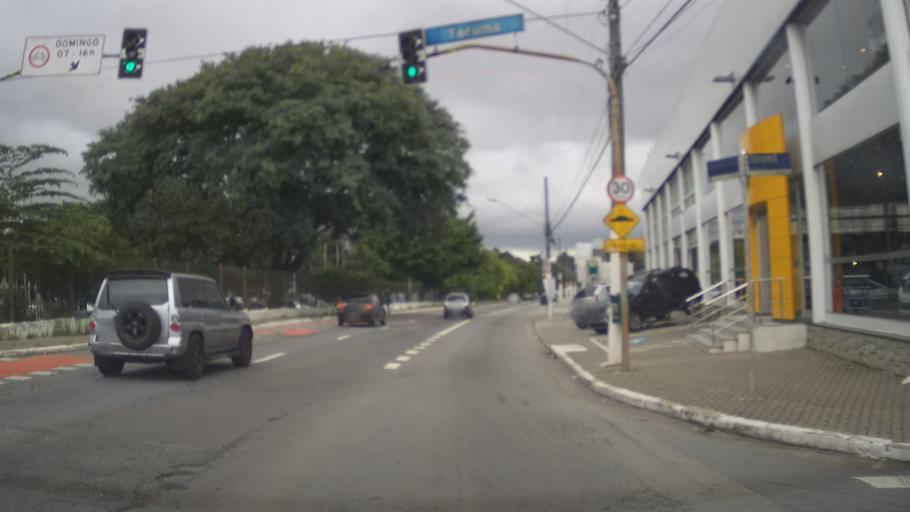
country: BR
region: Sao Paulo
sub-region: Guarulhos
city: Guarulhos
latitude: -23.5134
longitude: -46.5269
